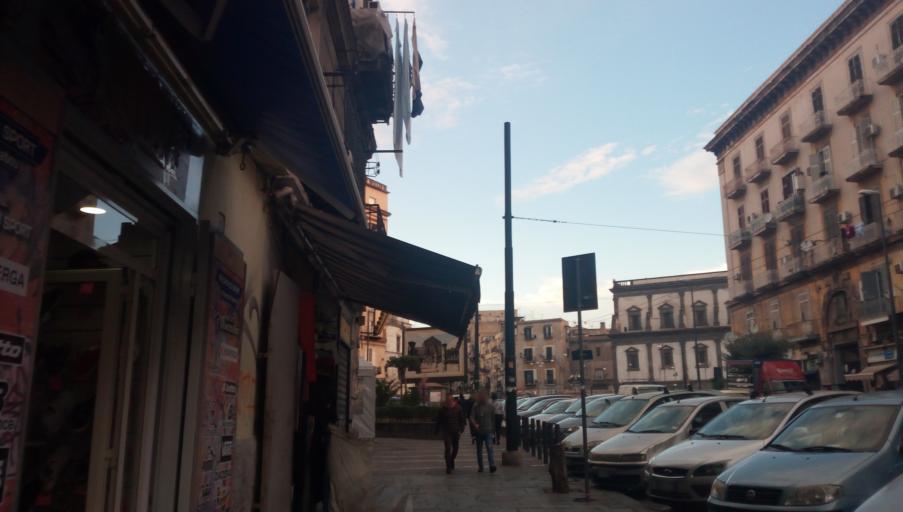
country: IT
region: Campania
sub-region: Provincia di Napoli
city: Napoli
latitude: 40.8533
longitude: 14.2660
